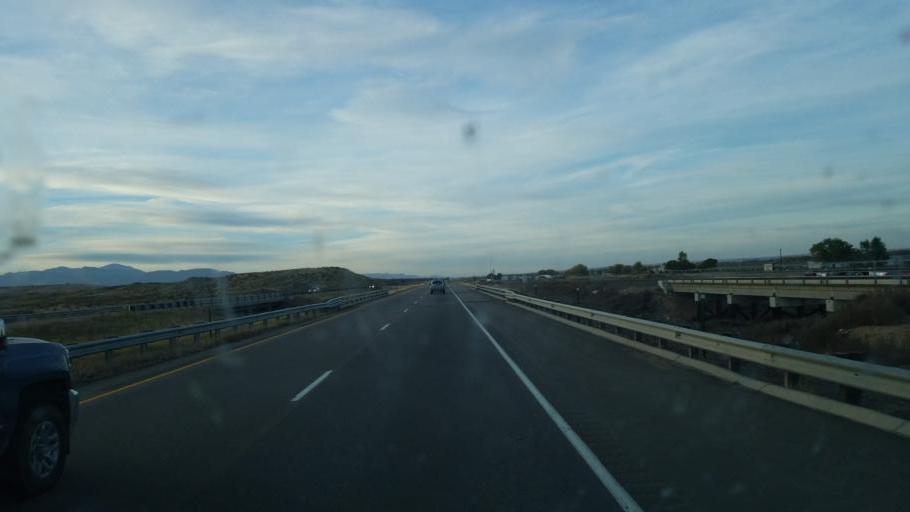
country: US
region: Colorado
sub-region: El Paso County
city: Fountain
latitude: 38.5339
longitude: -104.6382
